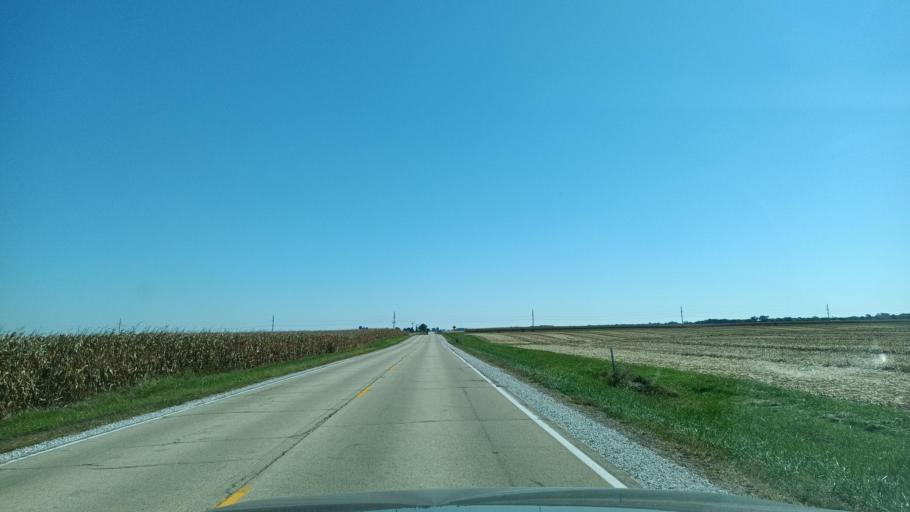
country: US
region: Illinois
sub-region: Peoria County
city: Elmwood
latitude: 40.9019
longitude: -89.9709
